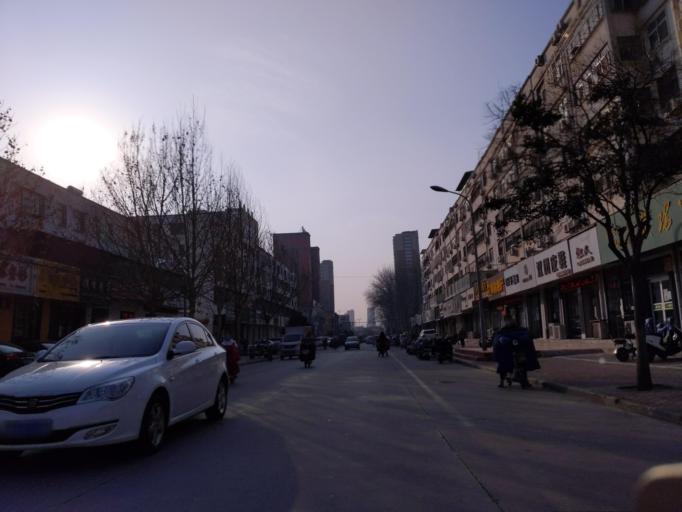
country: CN
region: Henan Sheng
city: Puyang
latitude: 35.7768
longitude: 115.0303
